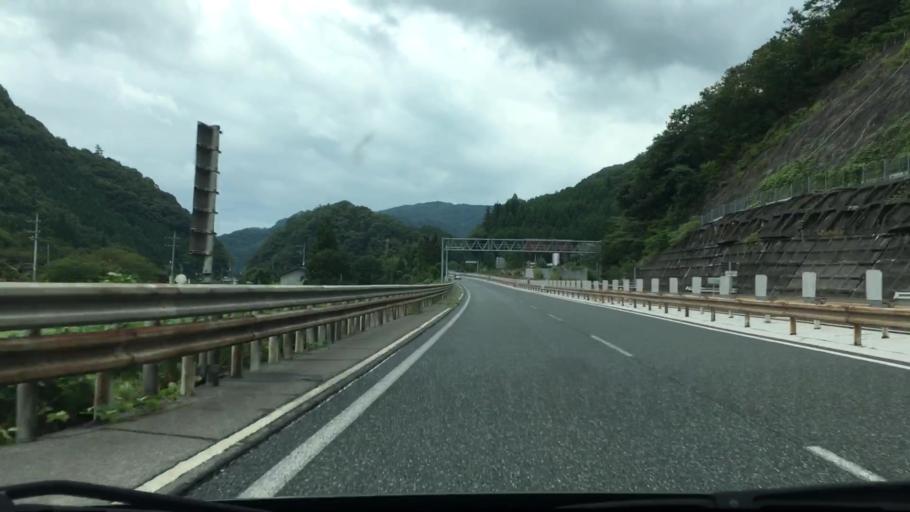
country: JP
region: Okayama
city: Niimi
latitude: 35.0037
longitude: 133.4741
